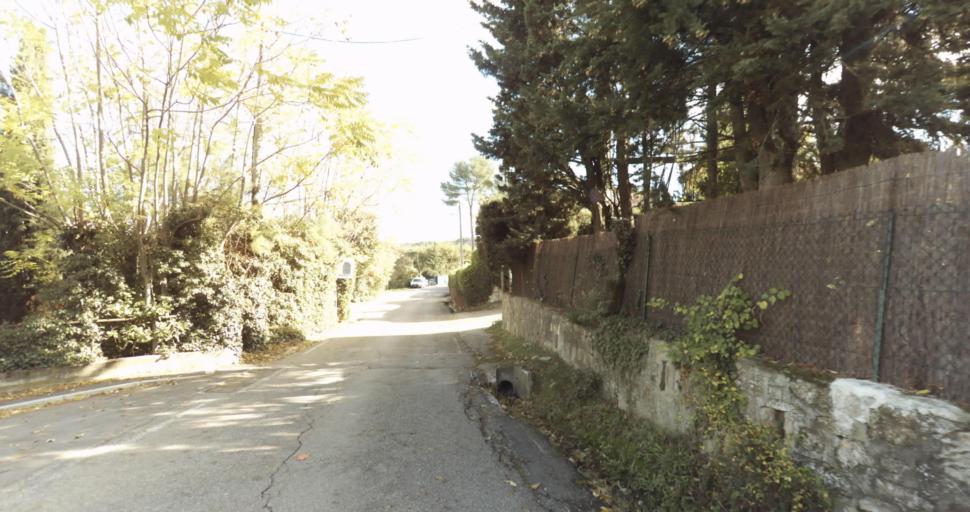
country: FR
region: Provence-Alpes-Cote d'Azur
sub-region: Departement des Bouches-du-Rhone
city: Venelles
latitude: 43.6023
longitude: 5.4834
